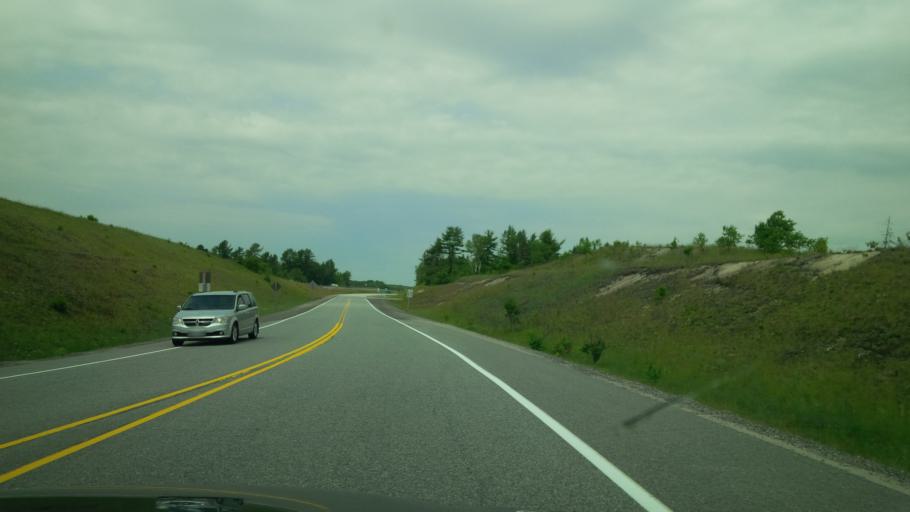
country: CA
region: Ontario
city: Huntsville
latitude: 45.5131
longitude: -79.3054
